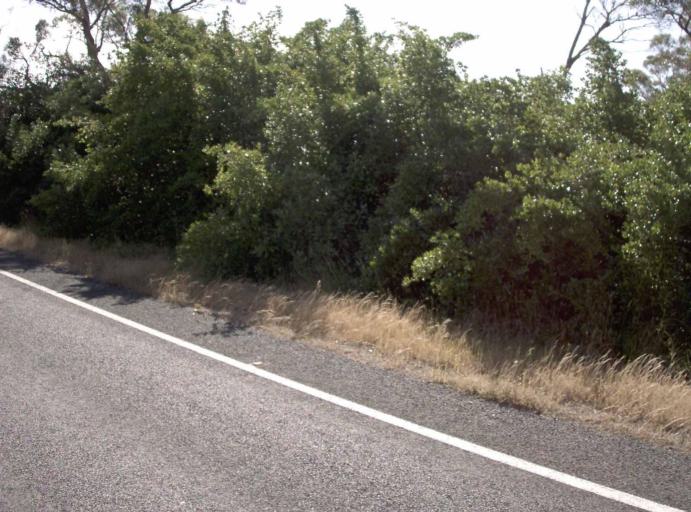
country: AU
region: Victoria
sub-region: Bass Coast
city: North Wonthaggi
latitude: -38.4314
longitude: 145.5008
